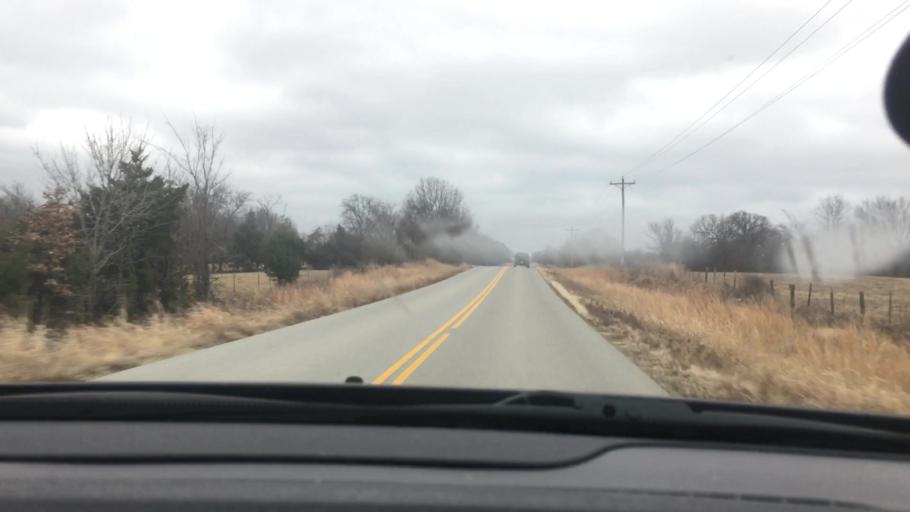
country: US
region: Oklahoma
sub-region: Atoka County
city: Atoka
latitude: 34.3229
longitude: -96.0755
